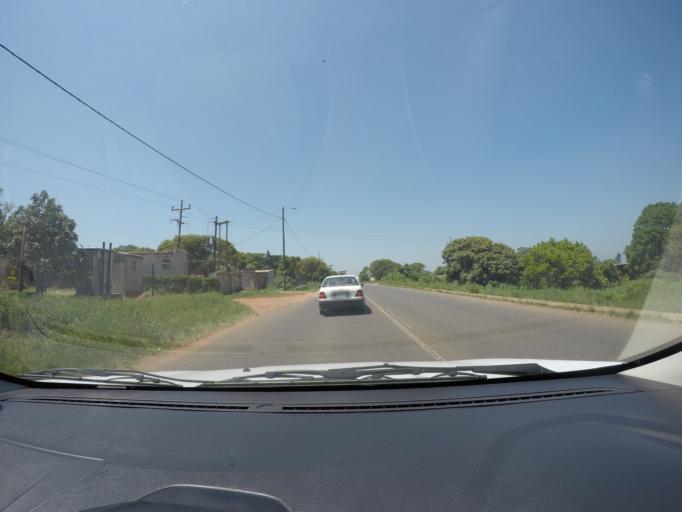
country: ZA
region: KwaZulu-Natal
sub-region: uThungulu District Municipality
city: eSikhawini
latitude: -28.8251
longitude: 31.9456
